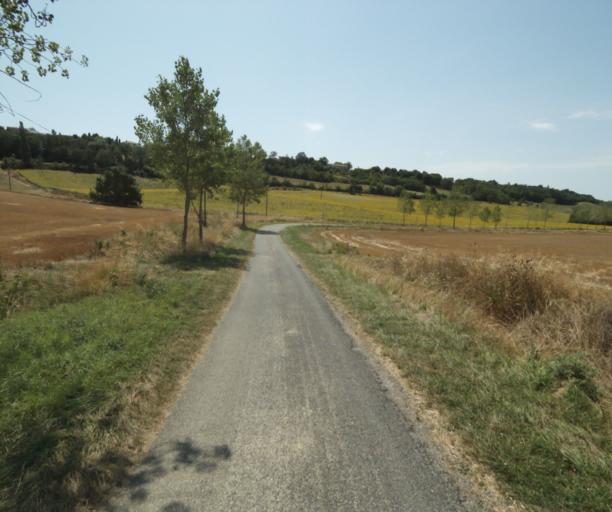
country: FR
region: Midi-Pyrenees
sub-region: Departement de la Haute-Garonne
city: Saint-Felix-Lauragais
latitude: 43.4531
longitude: 1.8866
